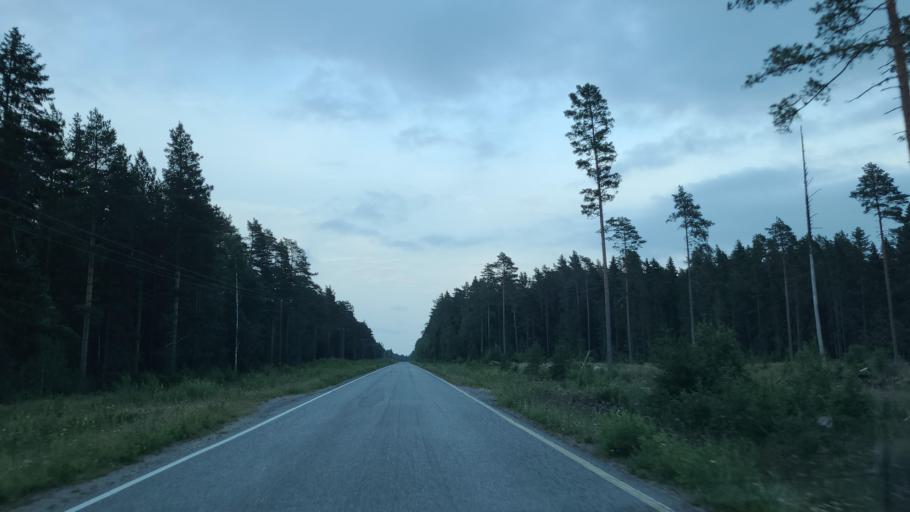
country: FI
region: Ostrobothnia
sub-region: Vaasa
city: Replot
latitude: 63.2034
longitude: 21.2752
